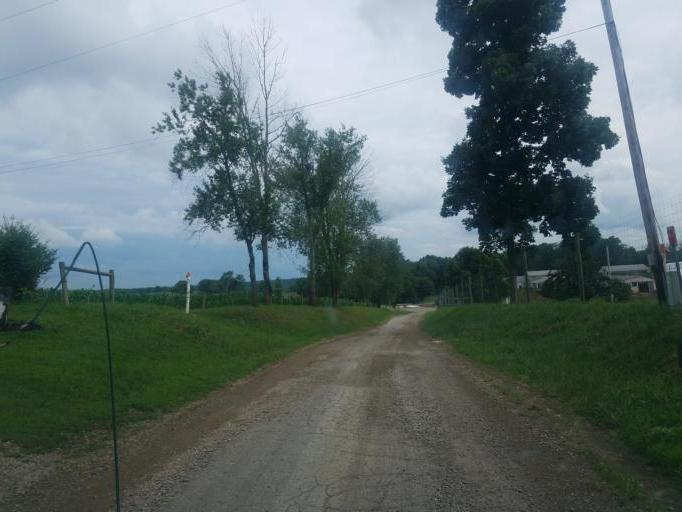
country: US
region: Ohio
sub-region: Knox County
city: Oak Hill
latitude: 40.3386
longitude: -82.1396
